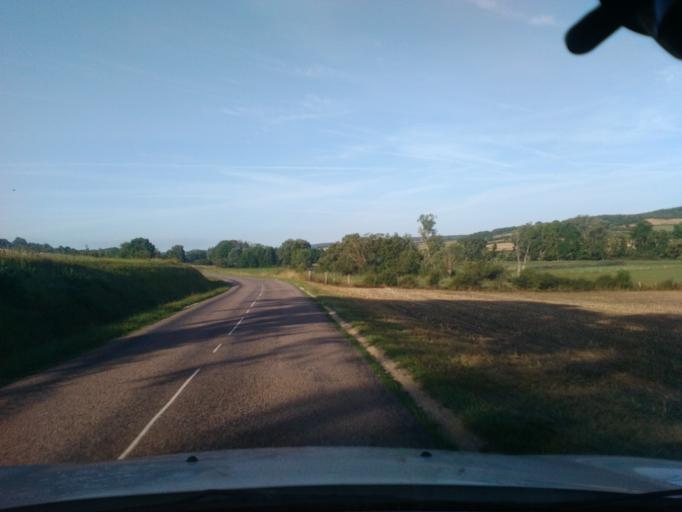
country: FR
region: Lorraine
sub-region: Departement des Vosges
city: Mirecourt
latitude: 48.2986
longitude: 6.0823
